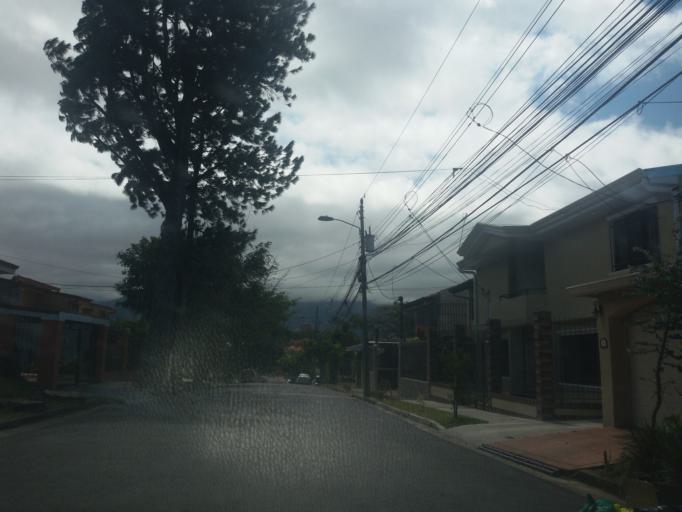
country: CR
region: San Jose
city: San Rafael
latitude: 9.9588
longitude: -84.1221
